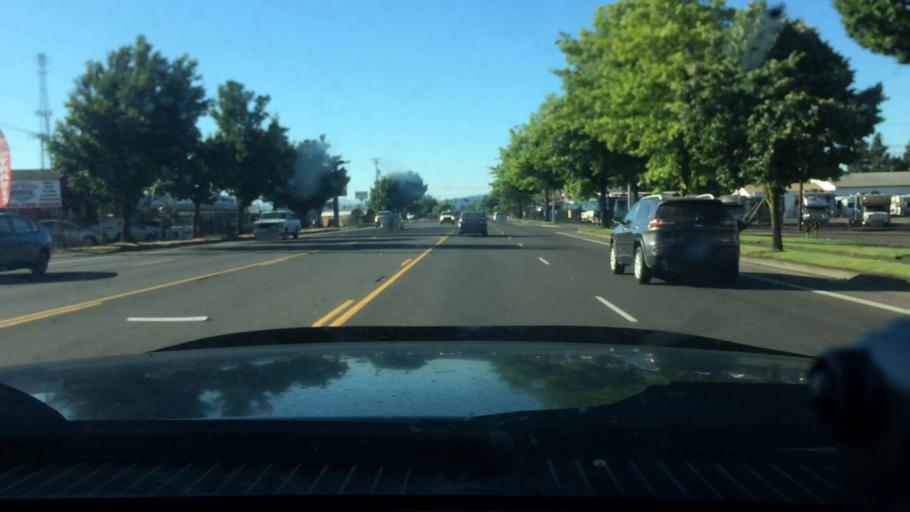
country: US
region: Oregon
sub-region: Lane County
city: Eugene
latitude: 44.0833
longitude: -123.1538
